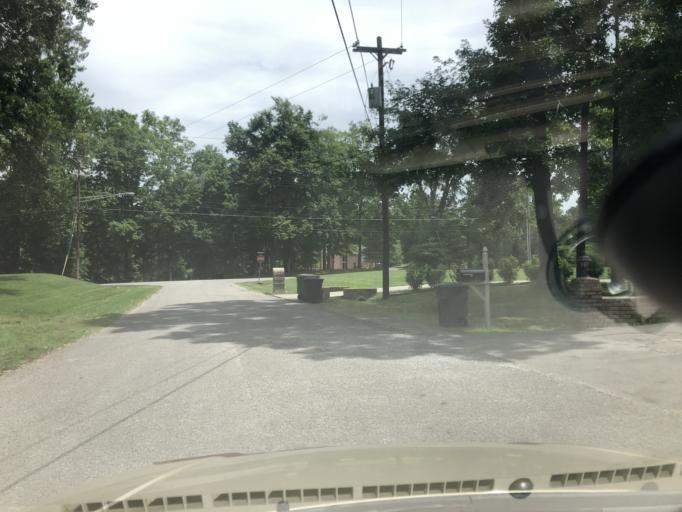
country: US
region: Tennessee
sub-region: Davidson County
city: Lakewood
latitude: 36.2525
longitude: -86.5913
